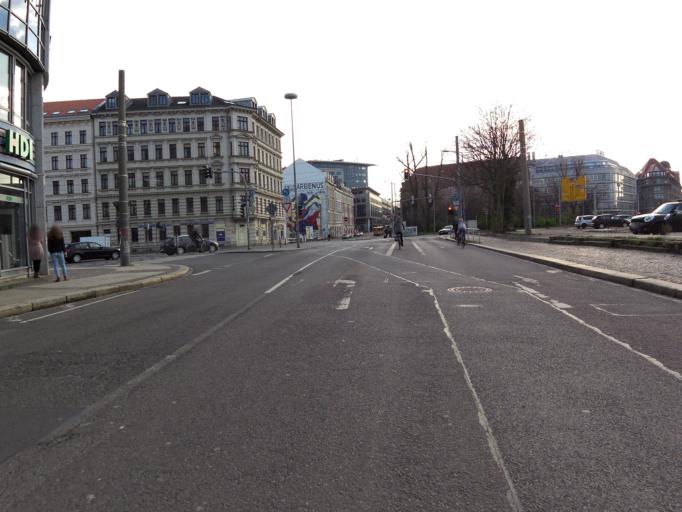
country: DE
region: Saxony
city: Leipzig
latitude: 51.3465
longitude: 12.3949
